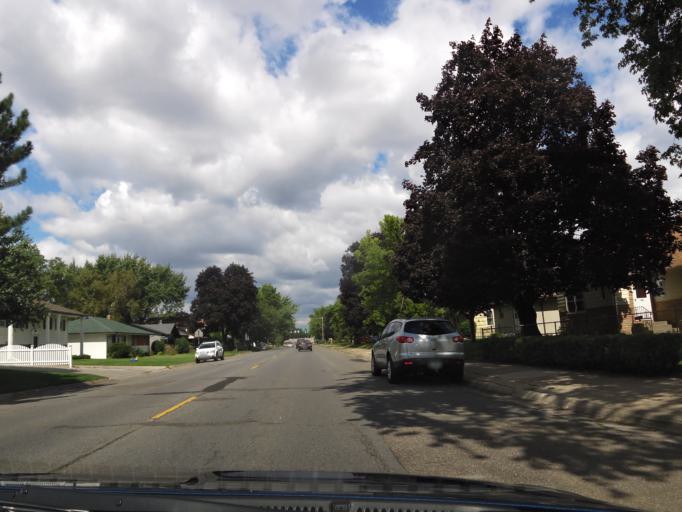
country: US
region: Minnesota
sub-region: Dakota County
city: Inver Grove Heights
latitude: 44.8709
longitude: -93.0424
